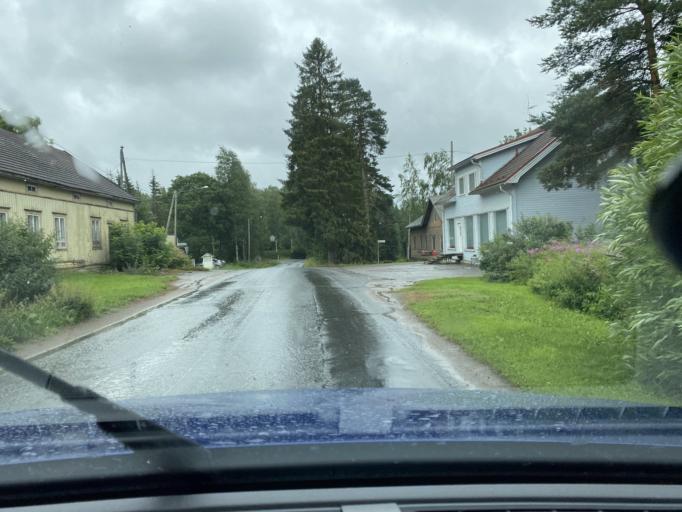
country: FI
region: Pirkanmaa
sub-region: Lounais-Pirkanmaa
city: Punkalaidun
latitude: 61.1475
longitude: 23.1935
